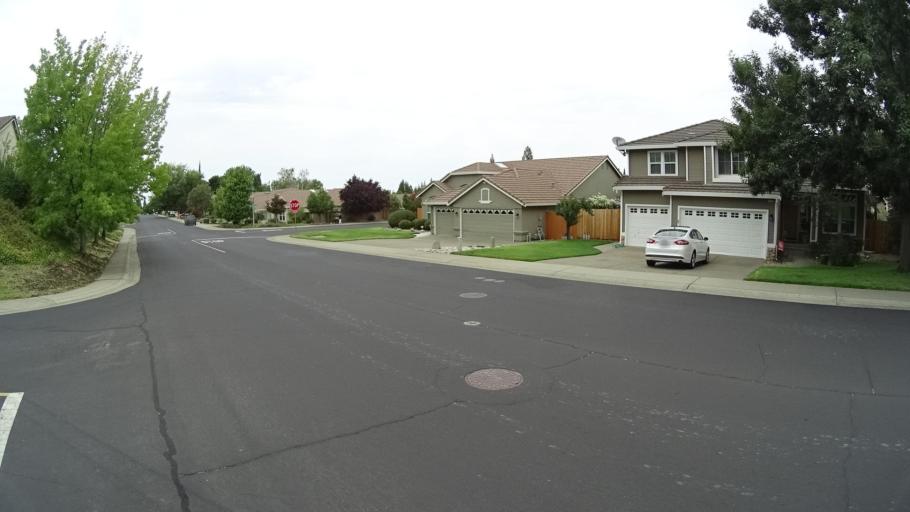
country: US
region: California
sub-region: Placer County
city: Rocklin
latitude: 38.7809
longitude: -121.2078
